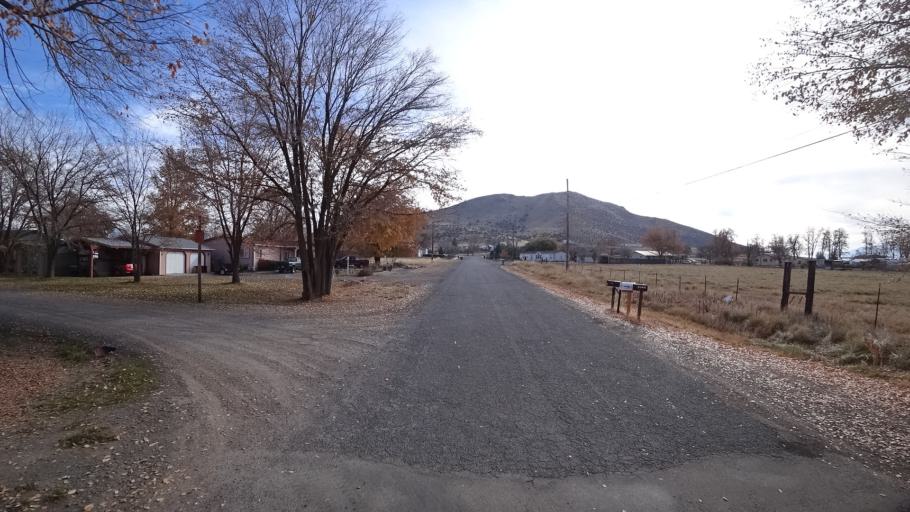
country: US
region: California
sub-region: Siskiyou County
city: Montague
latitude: 41.7213
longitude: -122.5253
